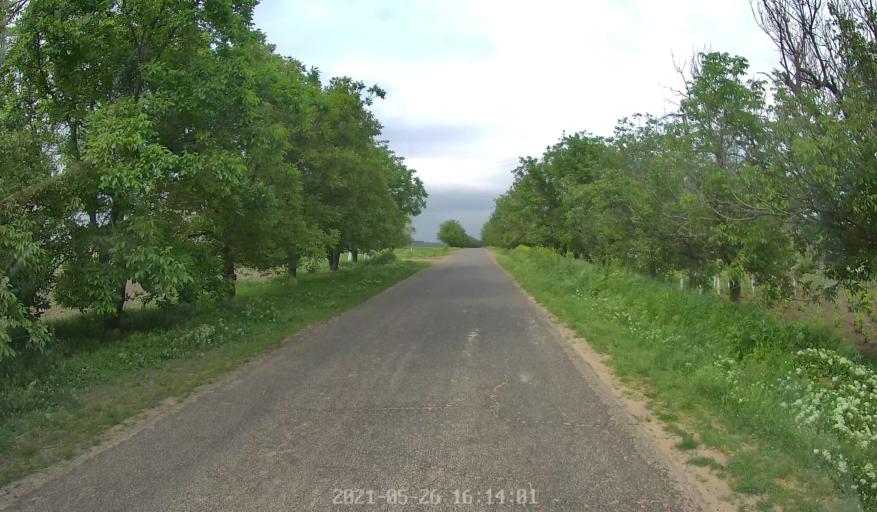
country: MD
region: Hincesti
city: Dancu
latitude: 46.7062
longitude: 28.3400
